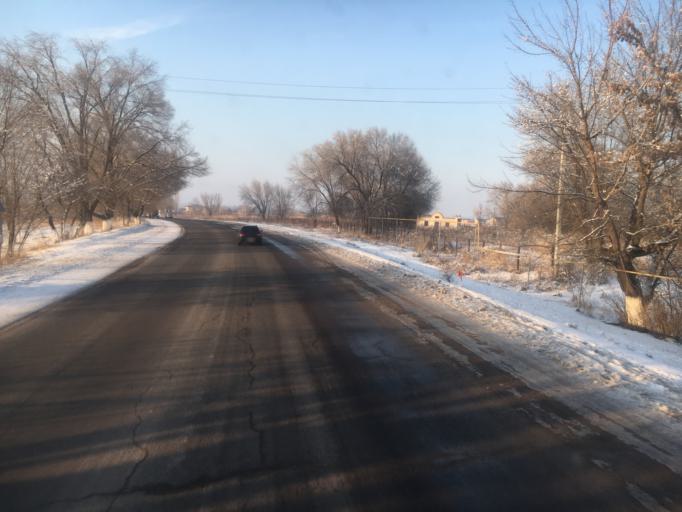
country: KZ
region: Almaty Oblysy
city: Burunday
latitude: 43.3404
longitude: 76.6587
